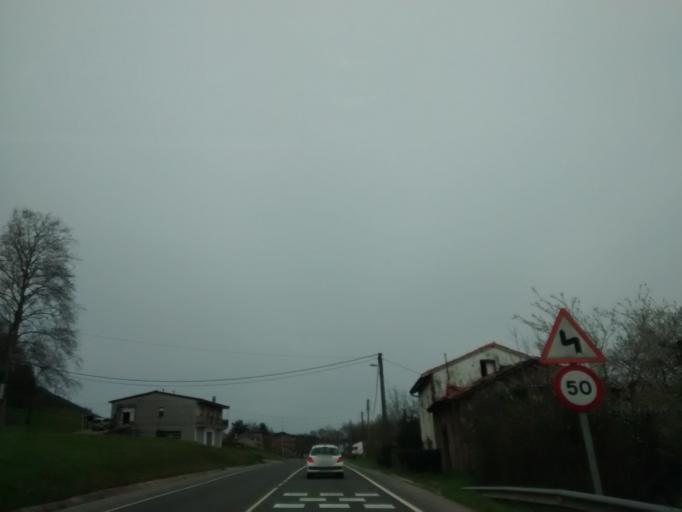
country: ES
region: Cantabria
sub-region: Provincia de Cantabria
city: Penagos
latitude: 43.3528
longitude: -3.7801
